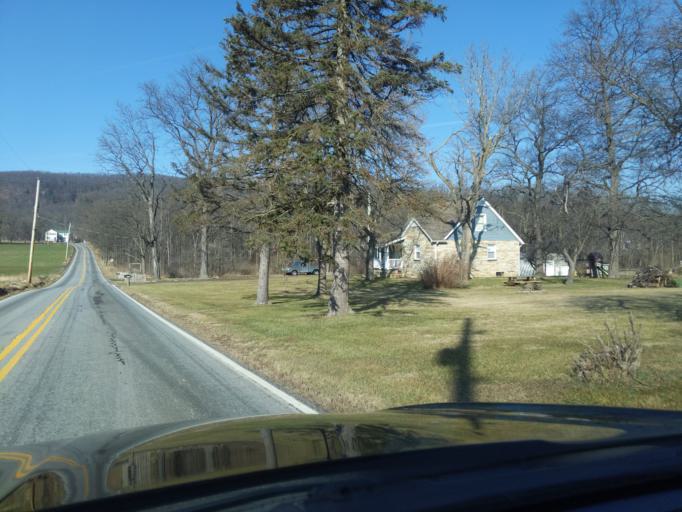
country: US
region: Pennsylvania
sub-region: Blair County
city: Tipton
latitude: 40.6166
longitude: -78.2602
